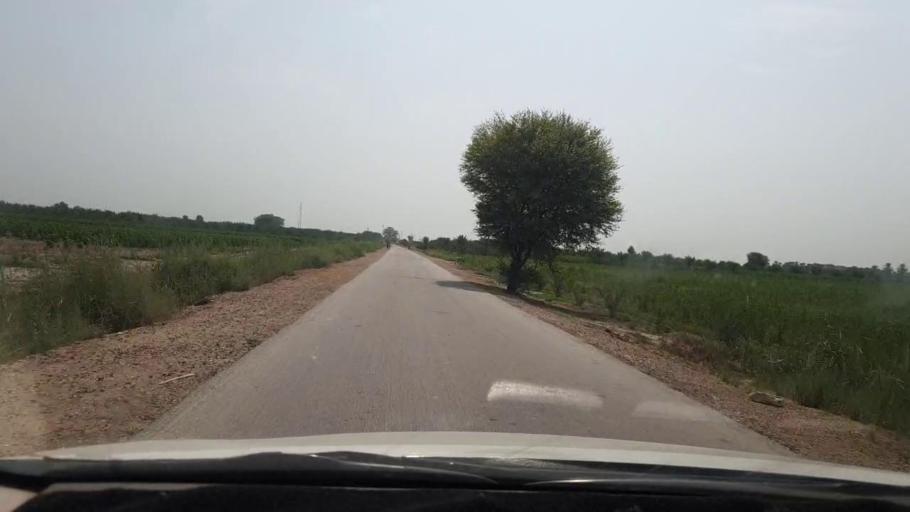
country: PK
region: Sindh
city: Rohri
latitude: 27.5384
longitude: 69.0223
